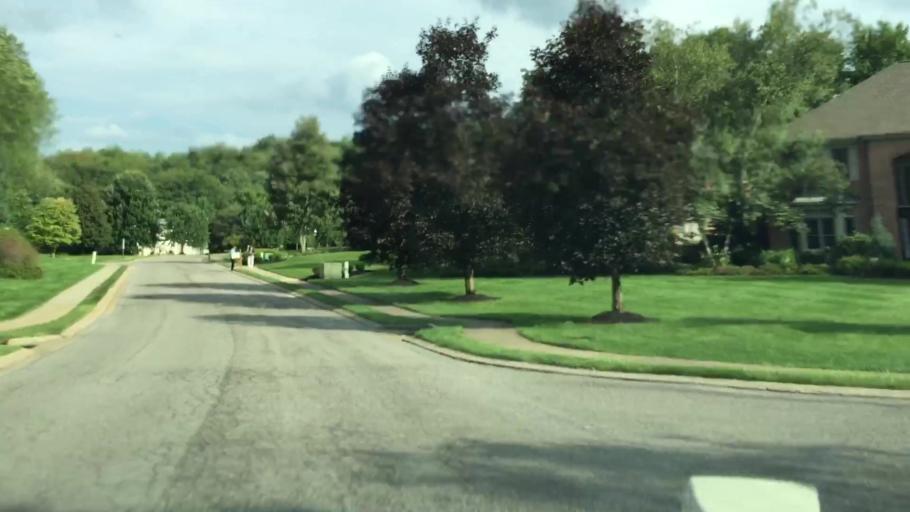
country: US
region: Pennsylvania
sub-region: Allegheny County
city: Franklin Park
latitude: 40.5764
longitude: -80.1118
